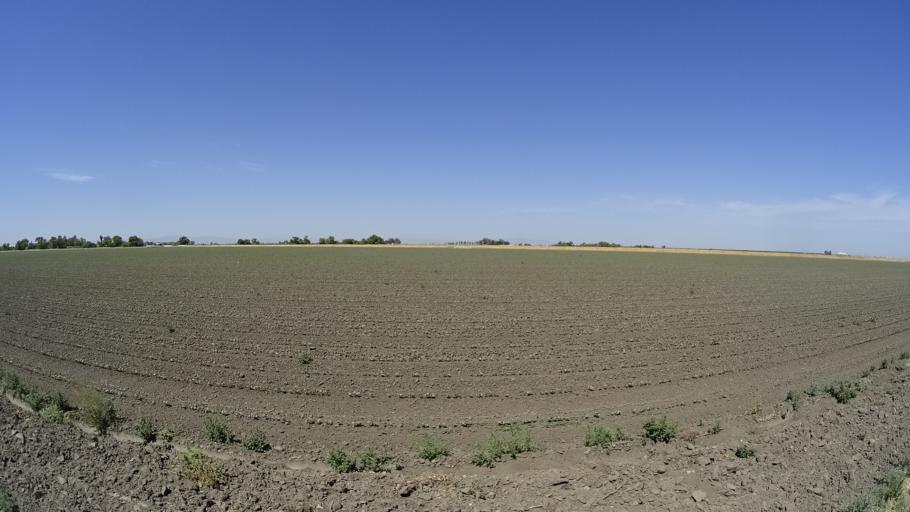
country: US
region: California
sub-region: Kings County
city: Stratford
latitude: 36.2019
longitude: -119.8161
